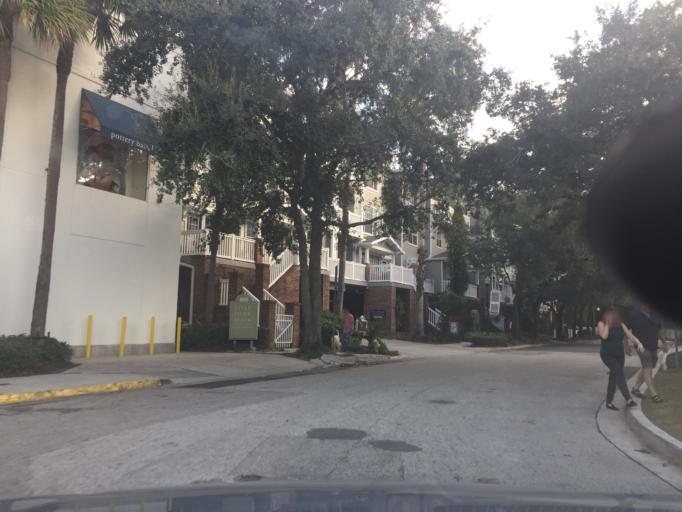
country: US
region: Florida
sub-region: Hillsborough County
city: Tampa
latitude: 27.9359
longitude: -82.4759
